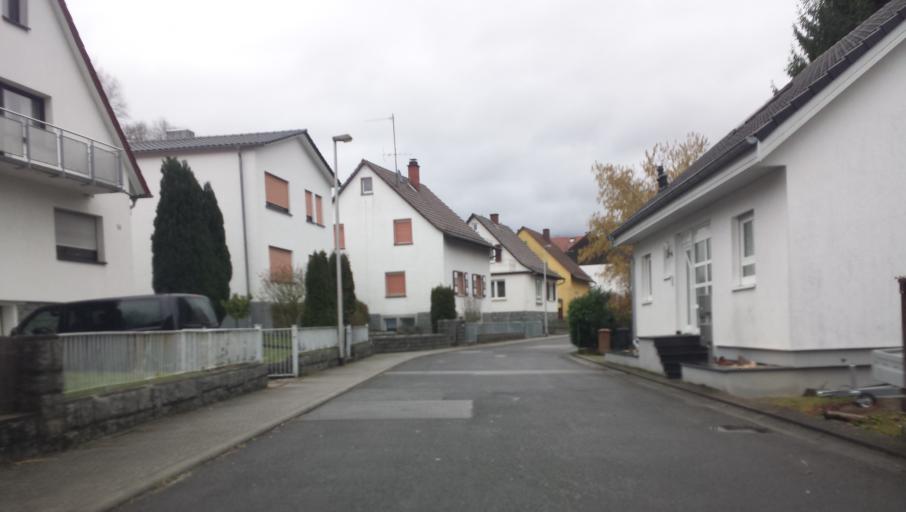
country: DE
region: Hesse
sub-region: Regierungsbezirk Darmstadt
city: Rimbach
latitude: 49.6252
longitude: 8.7651
